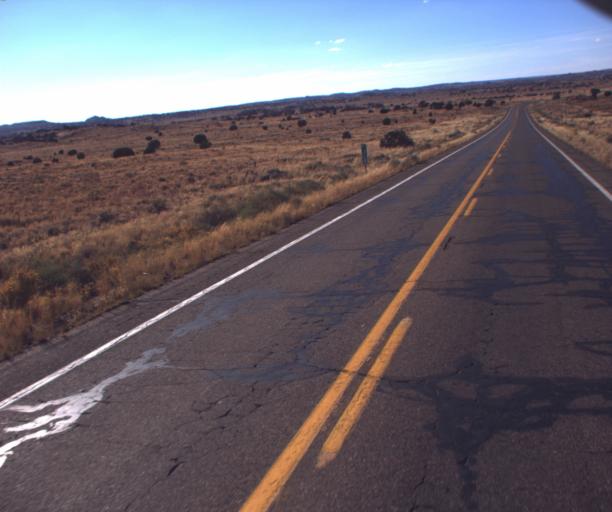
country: US
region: Arizona
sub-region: Coconino County
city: Kaibito
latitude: 36.5798
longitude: -111.1381
